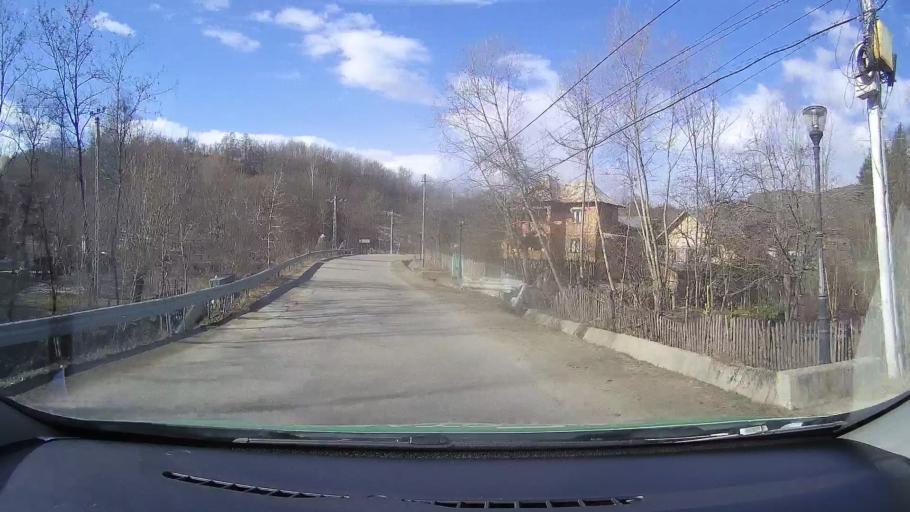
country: RO
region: Dambovita
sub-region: Comuna Varfuri
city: Varfuri
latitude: 45.0900
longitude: 25.4931
